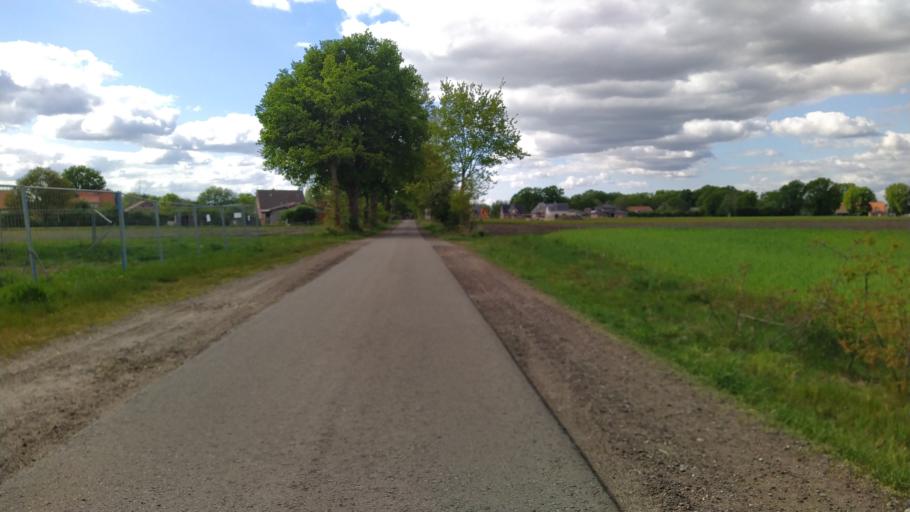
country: DE
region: Lower Saxony
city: Brest
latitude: 53.4463
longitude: 9.3915
